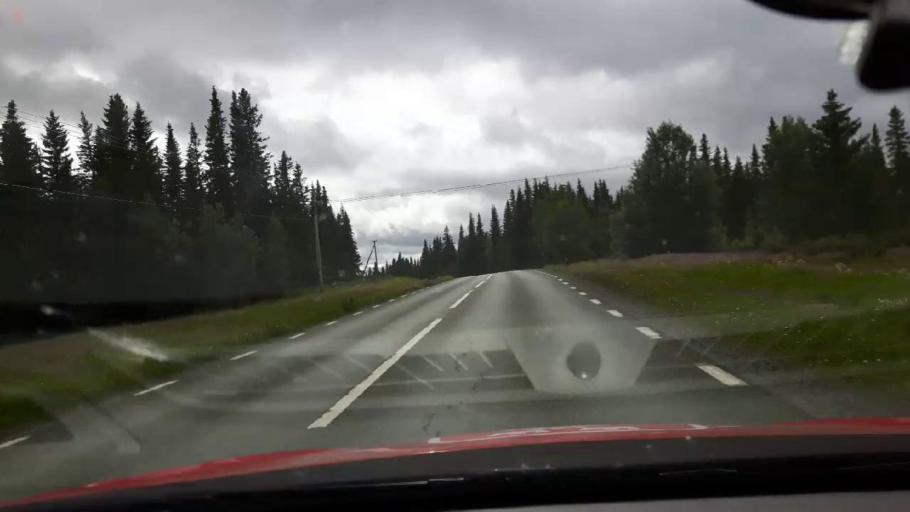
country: SE
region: Jaemtland
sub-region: Are Kommun
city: Are
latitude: 63.3751
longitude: 12.7132
